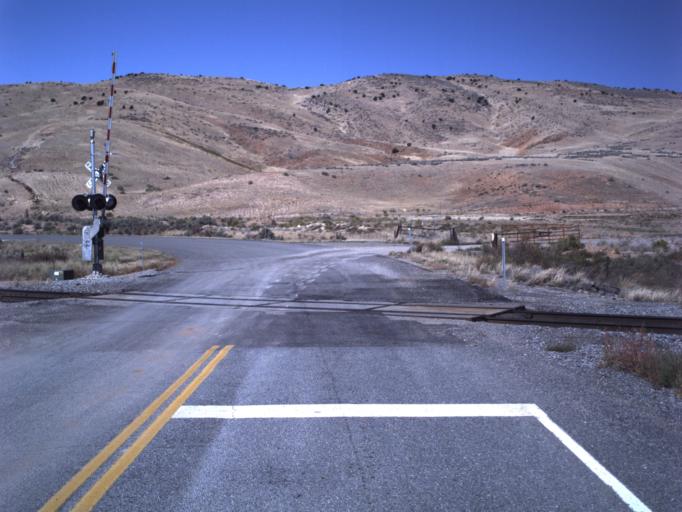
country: US
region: Utah
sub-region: Juab County
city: Nephi
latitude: 39.4856
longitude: -111.9820
